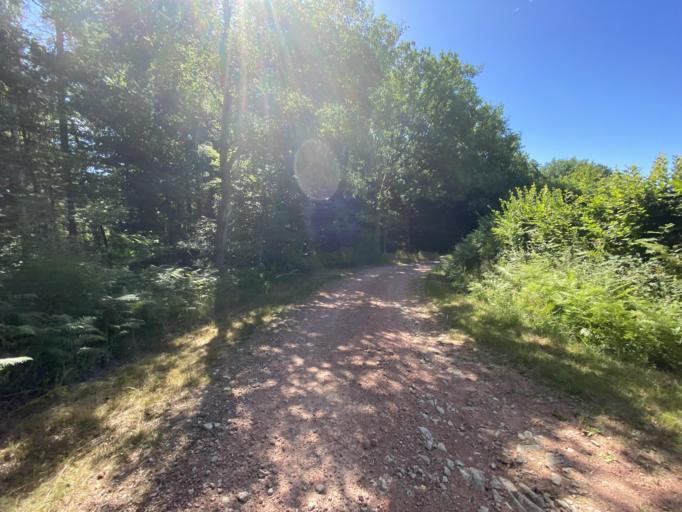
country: FR
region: Bourgogne
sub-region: Departement de la Cote-d'Or
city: Saulieu
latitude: 47.2908
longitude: 4.1286
